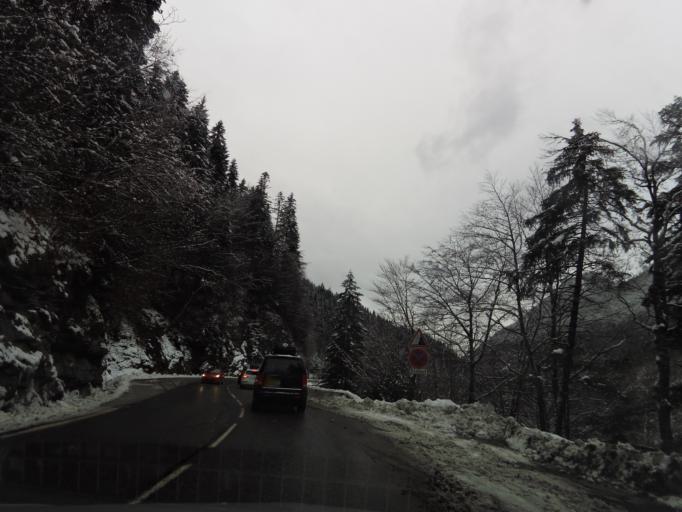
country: FR
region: Rhone-Alpes
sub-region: Departement de la Haute-Savoie
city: Taninges
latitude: 46.1221
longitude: 6.6186
